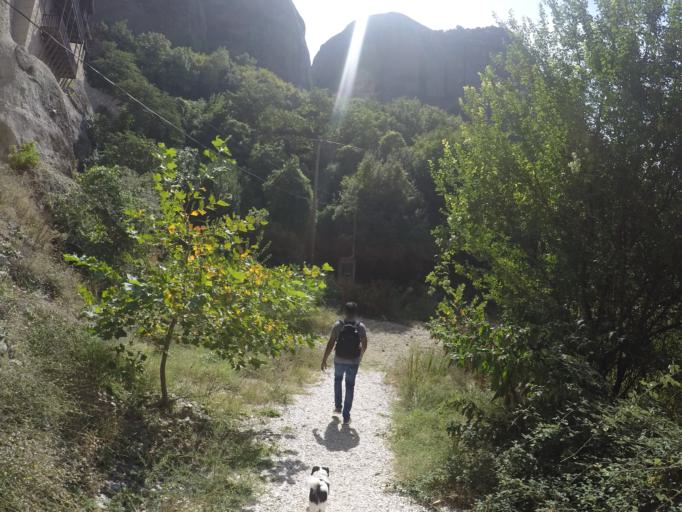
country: GR
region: Thessaly
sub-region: Trikala
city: Kastraki
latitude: 39.7117
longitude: 21.6207
